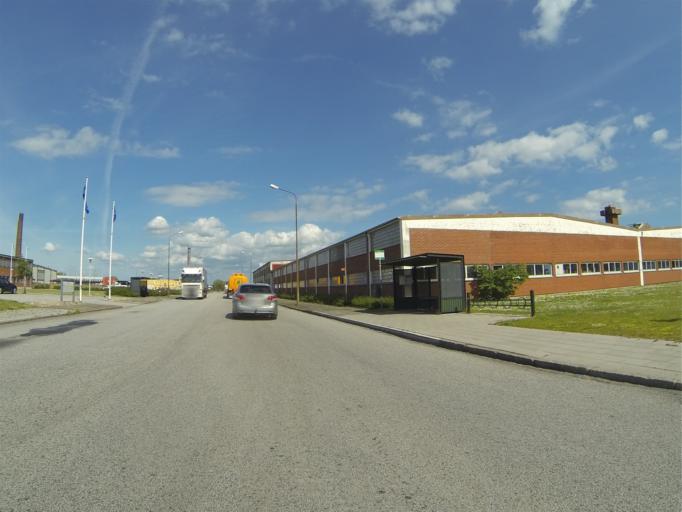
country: SE
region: Skane
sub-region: Malmo
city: Malmoe
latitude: 55.6191
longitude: 13.0323
